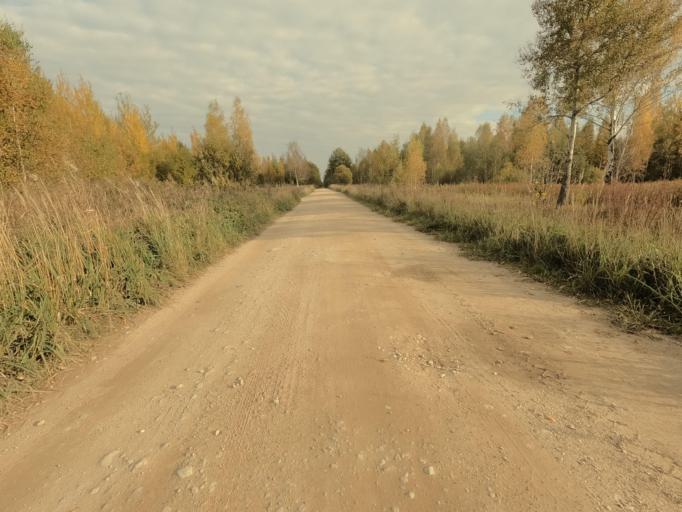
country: RU
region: Novgorod
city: Pankovka
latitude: 58.8962
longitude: 31.0053
